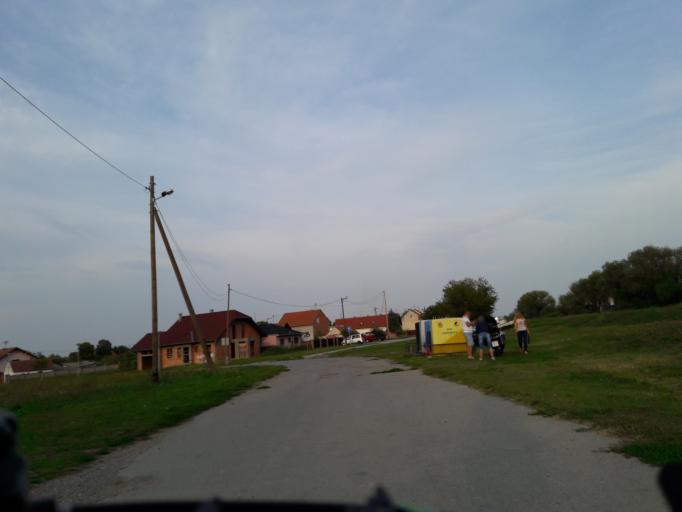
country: HR
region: Osjecko-Baranjska
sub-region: Grad Osijek
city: Osijek
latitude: 45.5614
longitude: 18.7057
